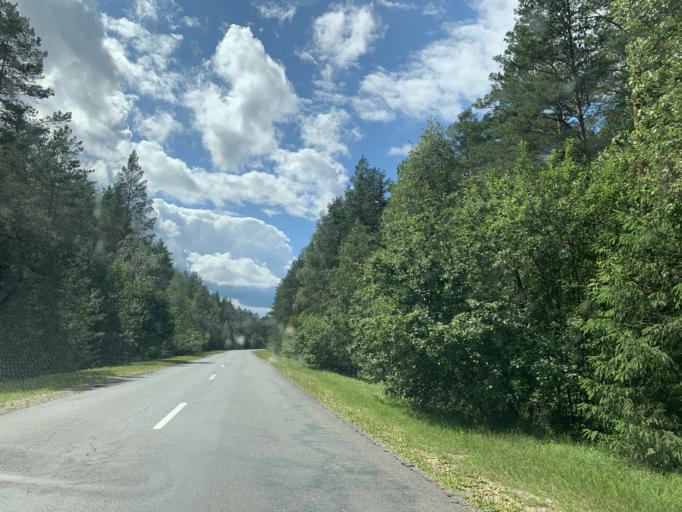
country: BY
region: Minsk
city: Rakaw
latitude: 53.9865
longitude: 26.9384
